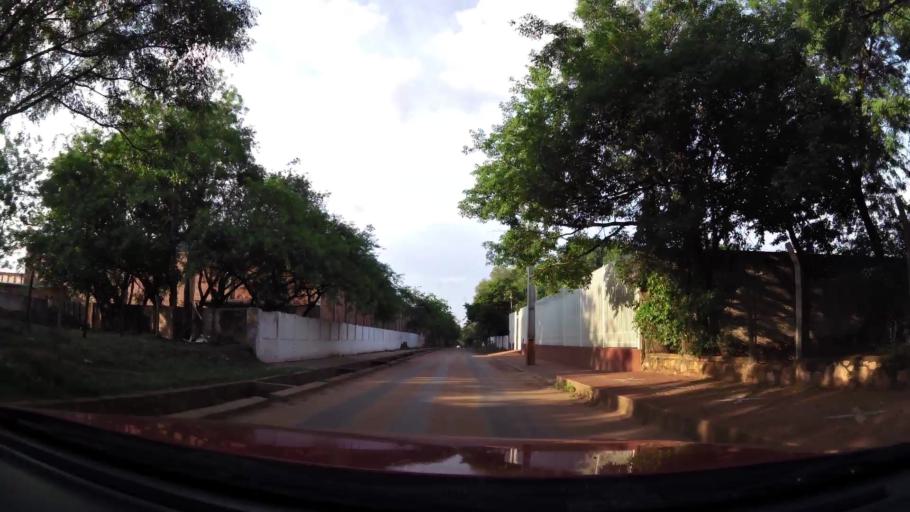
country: PY
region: Central
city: Fernando de la Mora
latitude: -25.3504
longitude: -57.5273
